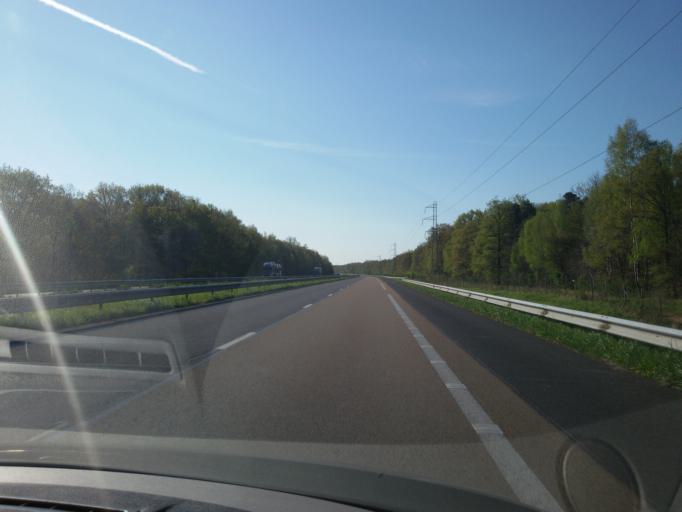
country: FR
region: Centre
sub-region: Departement du Loiret
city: Courtenay
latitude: 48.0941
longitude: 3.0338
